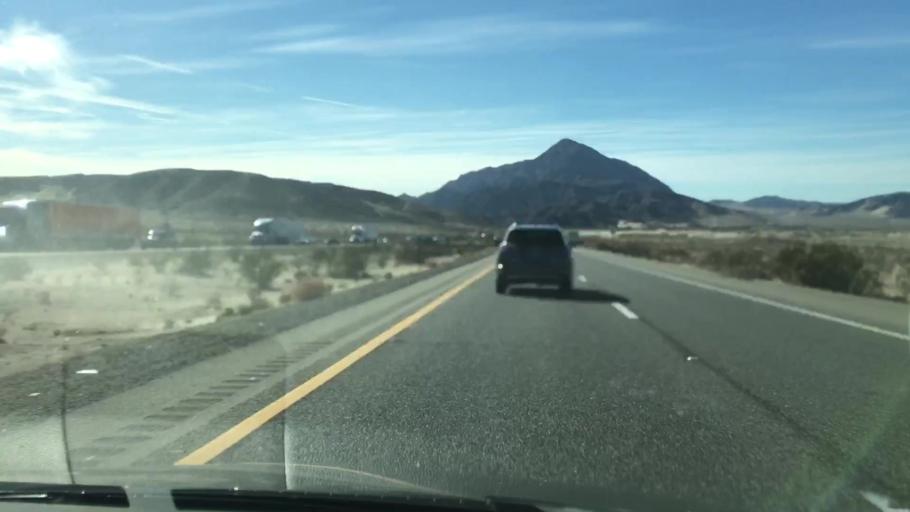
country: US
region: California
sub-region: San Bernardino County
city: Fort Irwin
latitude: 35.1109
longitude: -116.2485
